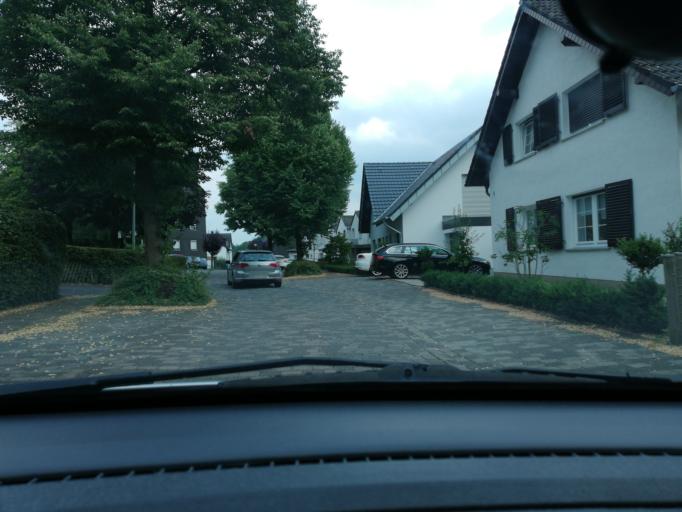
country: DE
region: North Rhine-Westphalia
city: Wetter (Ruhr)
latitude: 51.3719
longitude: 7.3677
